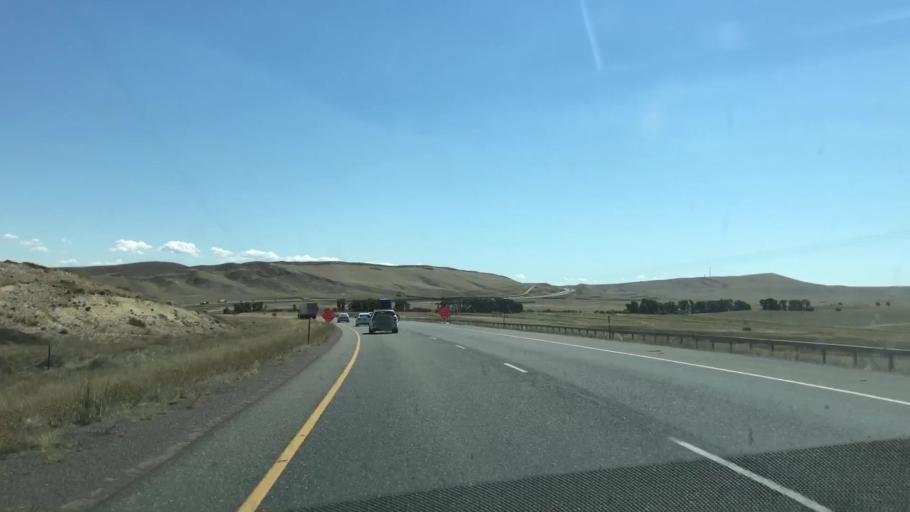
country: US
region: Wyoming
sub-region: Albany County
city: Laramie
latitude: 41.5287
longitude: -106.0695
